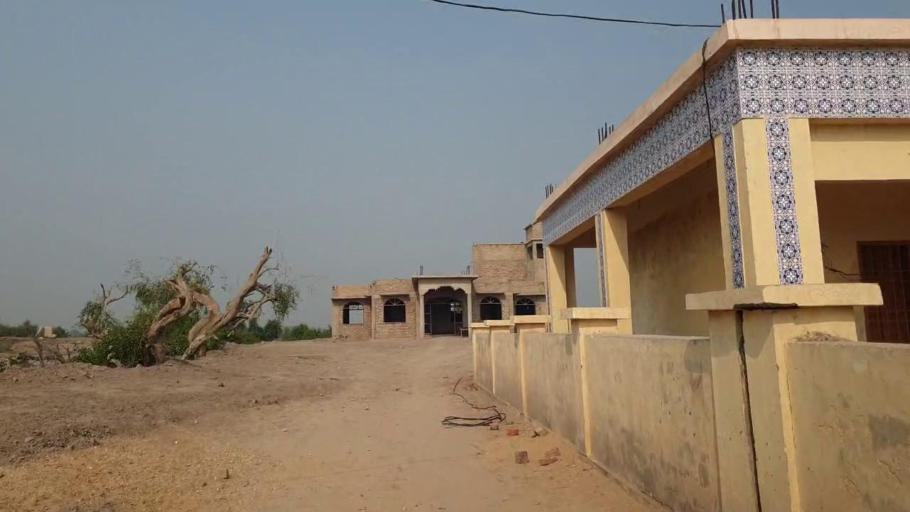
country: PK
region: Sindh
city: Bhan
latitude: 26.5106
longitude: 67.7266
